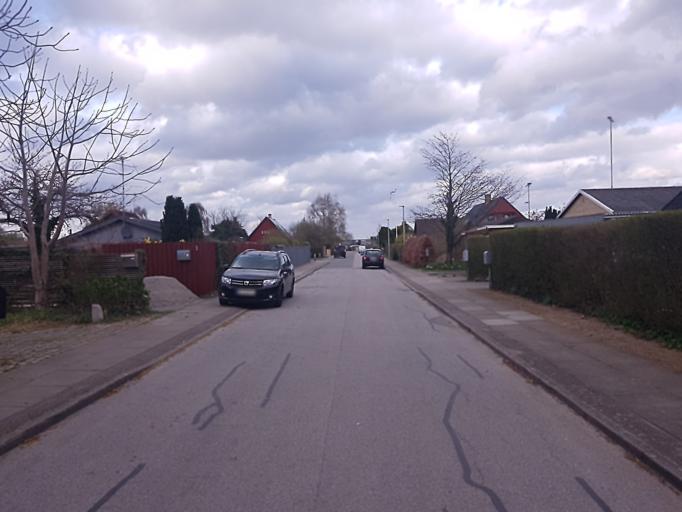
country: DK
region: Capital Region
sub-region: Tarnby Kommune
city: Tarnby
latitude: 55.6156
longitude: 12.6015
